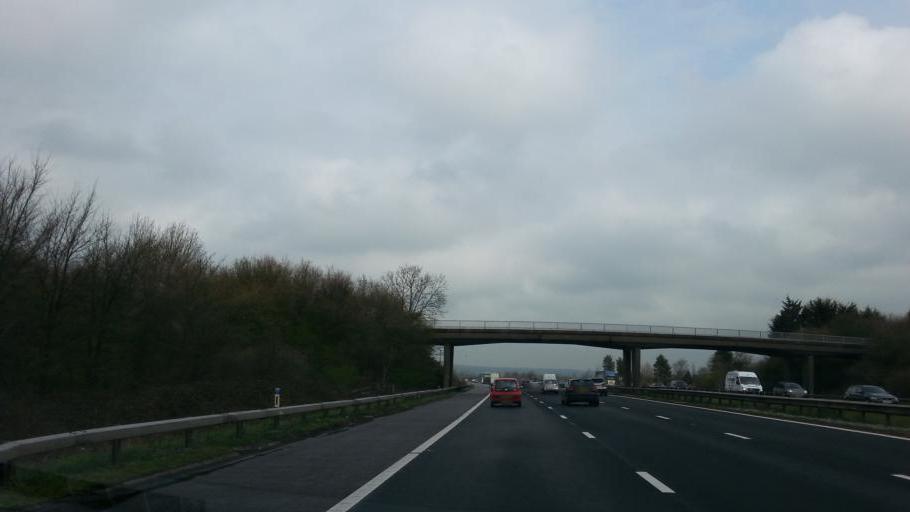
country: GB
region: England
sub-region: North Somerset
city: Kingston Seymour
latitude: 51.3971
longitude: -2.8564
